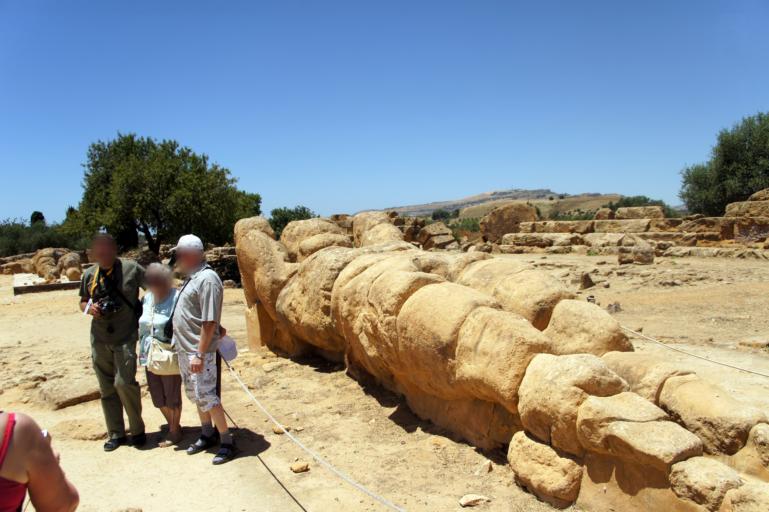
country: IT
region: Sicily
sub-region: Agrigento
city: Villaseta
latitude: 37.2907
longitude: 13.5854
